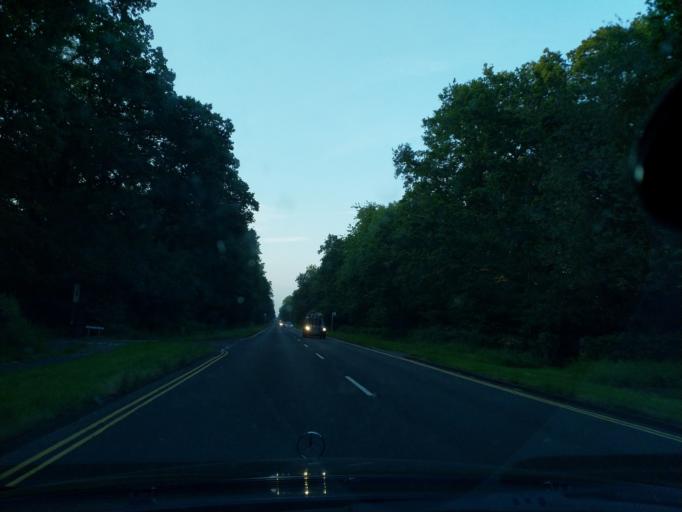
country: GB
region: England
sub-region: Coventry
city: Coventry
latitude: 52.3760
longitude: -1.5450
